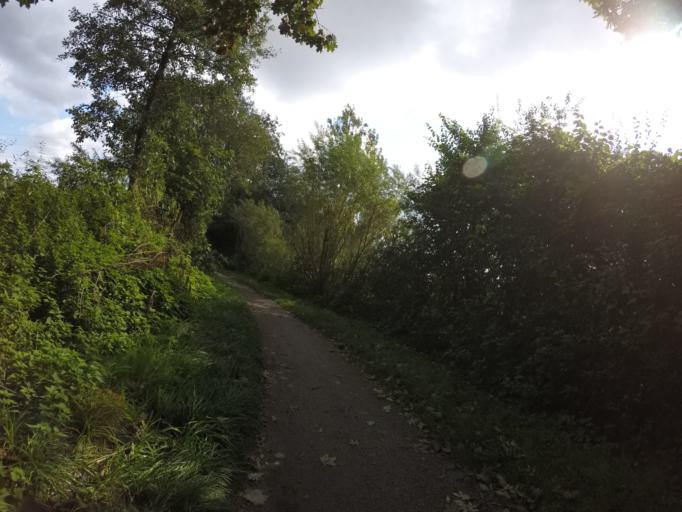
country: DE
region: North Rhine-Westphalia
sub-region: Regierungsbezirk Detmold
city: Hiddenhausen
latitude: 52.1421
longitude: 8.6208
